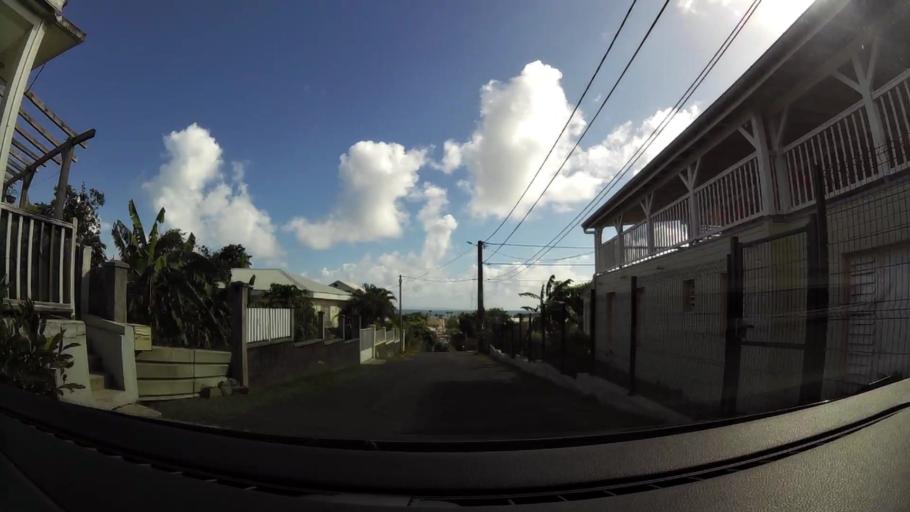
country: GP
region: Guadeloupe
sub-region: Guadeloupe
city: Sainte-Anne
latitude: 16.2283
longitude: -61.3838
